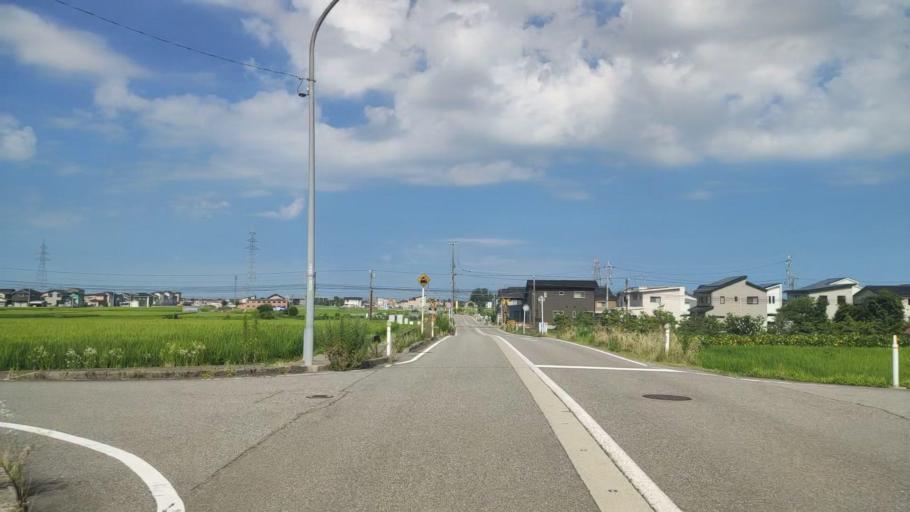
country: JP
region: Ishikawa
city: Tsurugi-asahimachi
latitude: 36.4735
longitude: 136.6125
